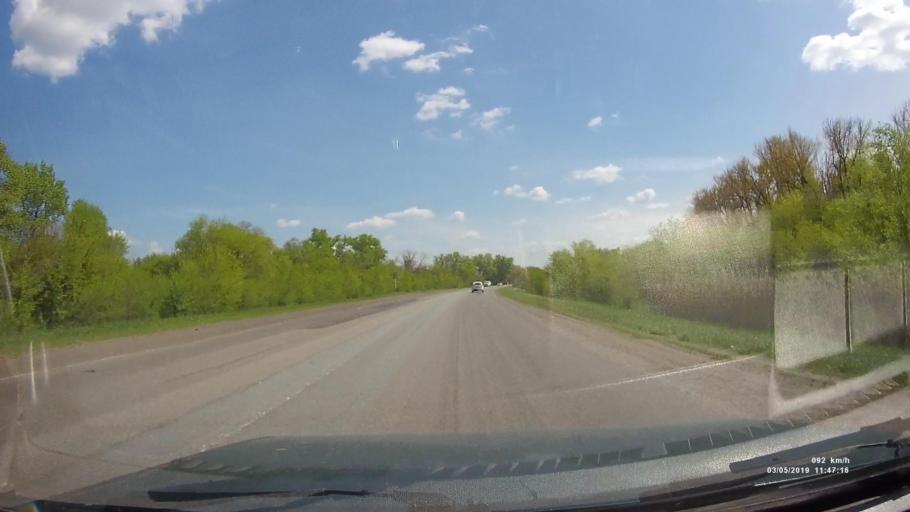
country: RU
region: Rostov
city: Starocherkasskaya
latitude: 47.1510
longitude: 40.1366
